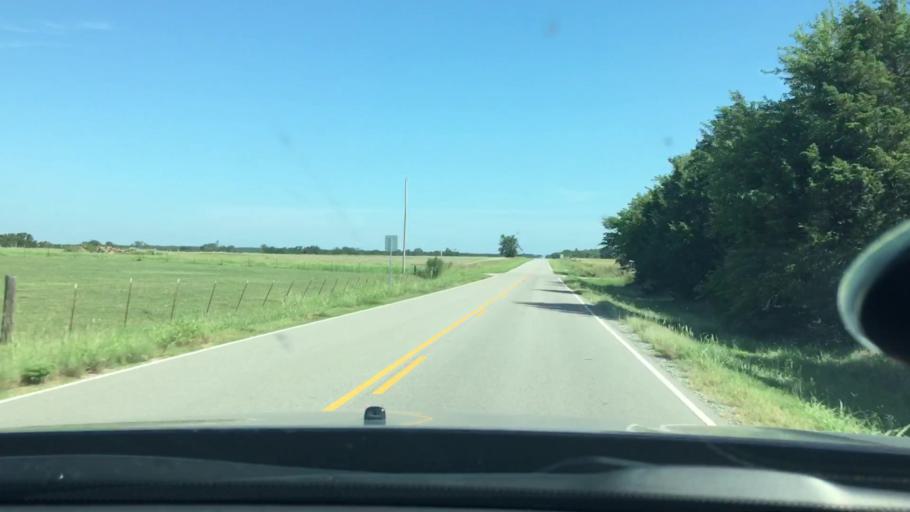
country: US
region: Oklahoma
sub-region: Johnston County
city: Tishomingo
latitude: 34.3022
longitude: -96.5488
